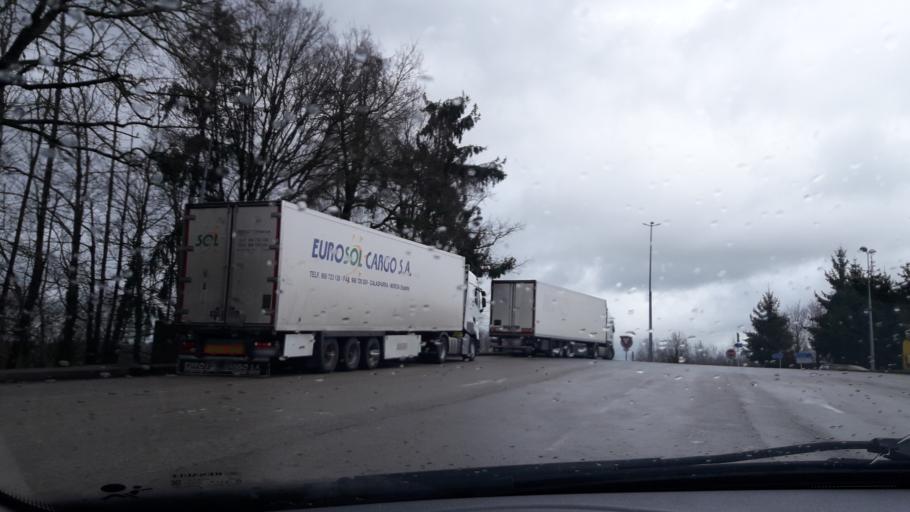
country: FR
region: Limousin
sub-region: Departement de la Haute-Vienne
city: Saint-Germain-les-Belles
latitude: 45.5427
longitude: 1.5083
